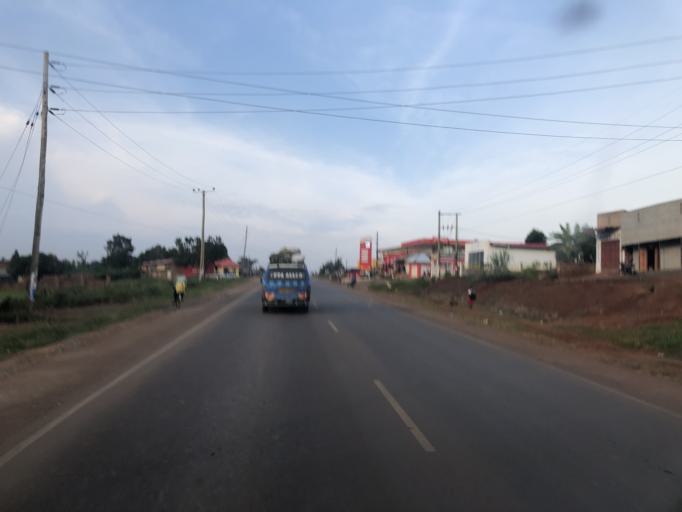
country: UG
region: Central Region
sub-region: Wakiso District
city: Kajansi
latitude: 0.2655
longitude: 32.4311
